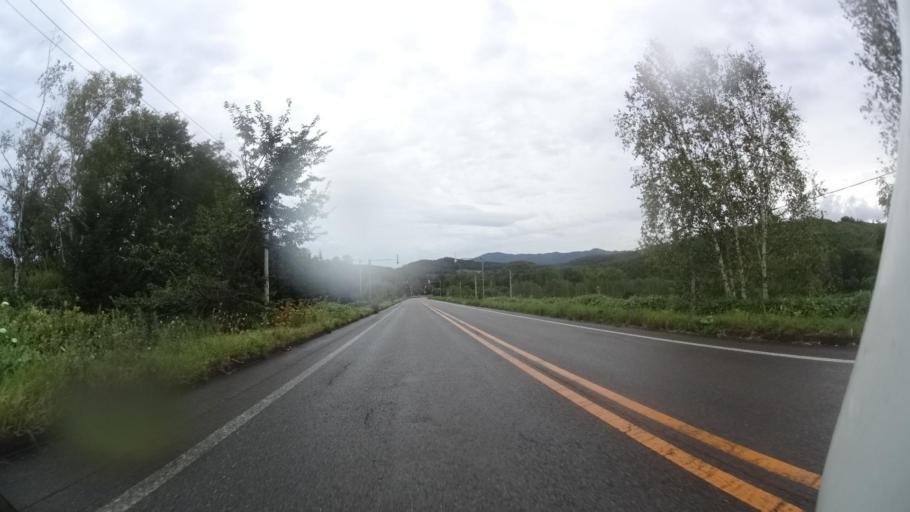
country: JP
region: Hokkaido
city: Kitami
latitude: 44.0916
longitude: 143.7490
